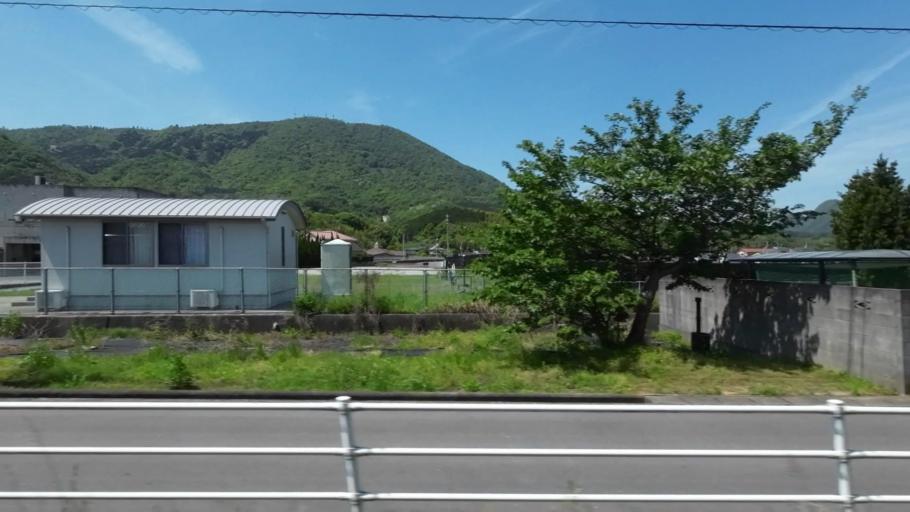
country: JP
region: Kagawa
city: Marugame
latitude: 34.2121
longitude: 133.8022
